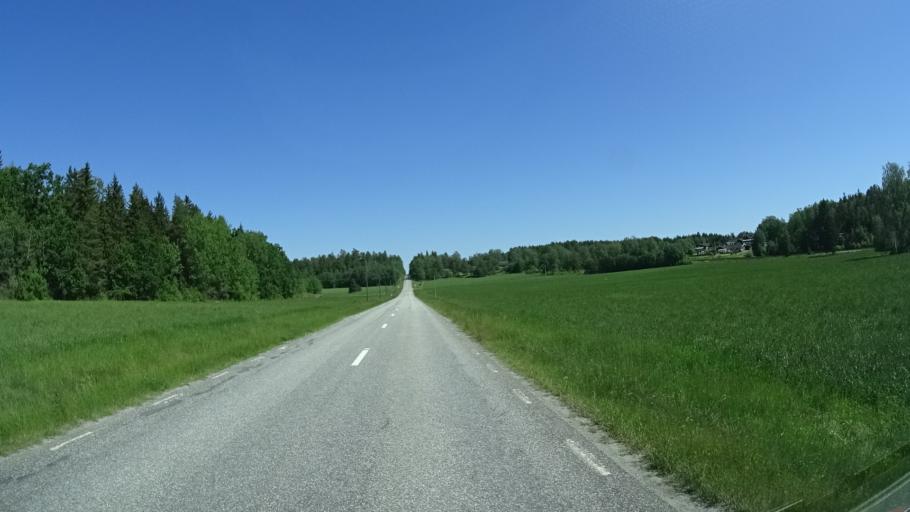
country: SE
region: Stockholm
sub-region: Vallentuna Kommun
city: Vallentuna
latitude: 59.6032
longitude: 18.1343
